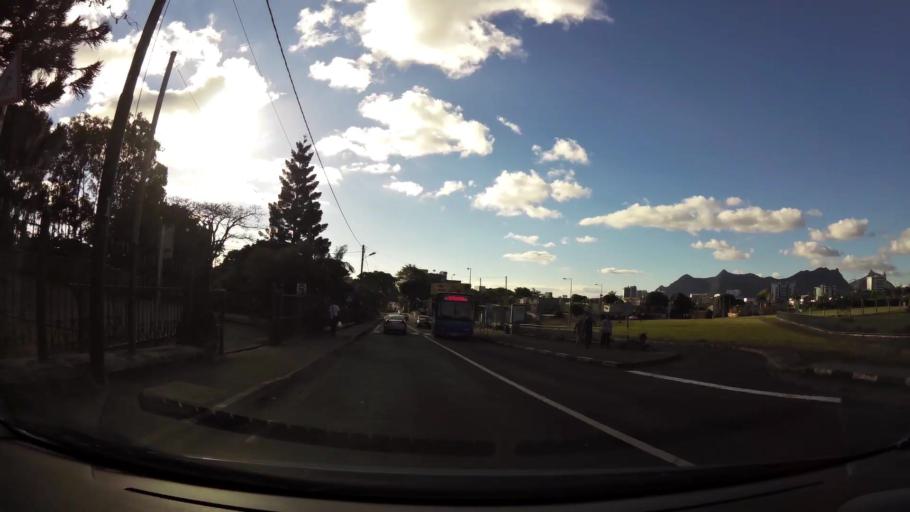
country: MU
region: Plaines Wilhems
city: Quatre Bornes
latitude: -20.2559
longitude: 57.4872
